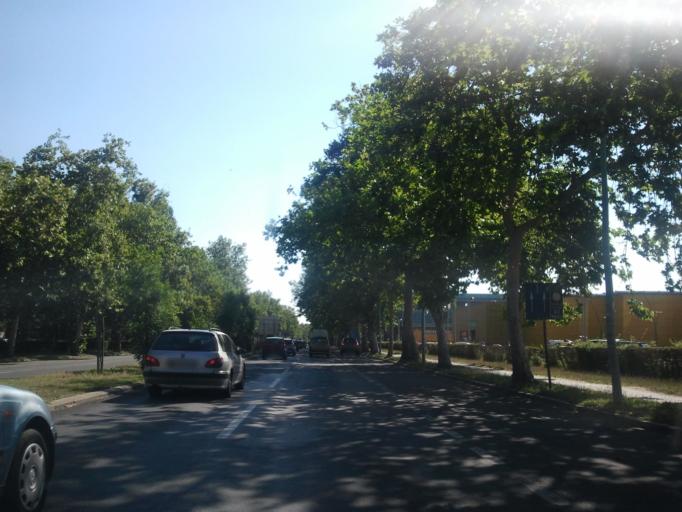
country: RS
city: Veternik
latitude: 45.2447
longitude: 19.7962
